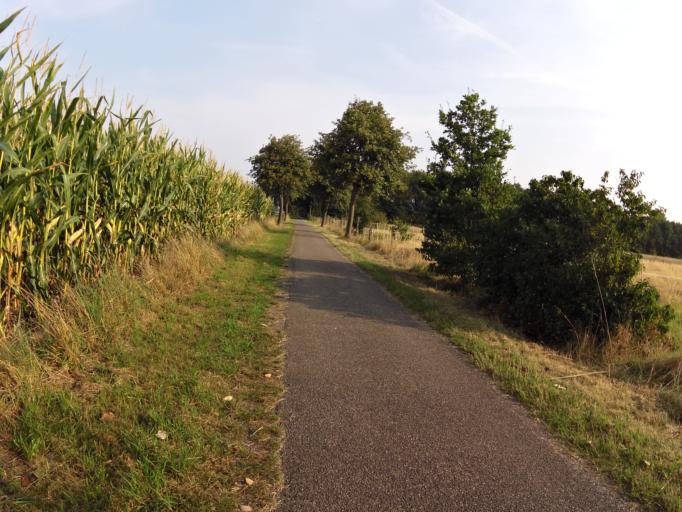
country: DE
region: North Rhine-Westphalia
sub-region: Regierungsbezirk Detmold
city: Petershagen
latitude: 52.3965
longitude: 8.9642
